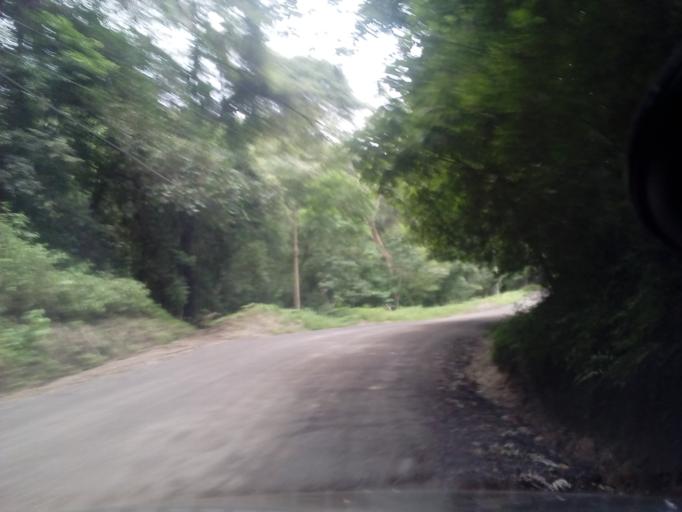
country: CR
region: Guanacaste
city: Samara
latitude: 9.9203
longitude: -85.5407
